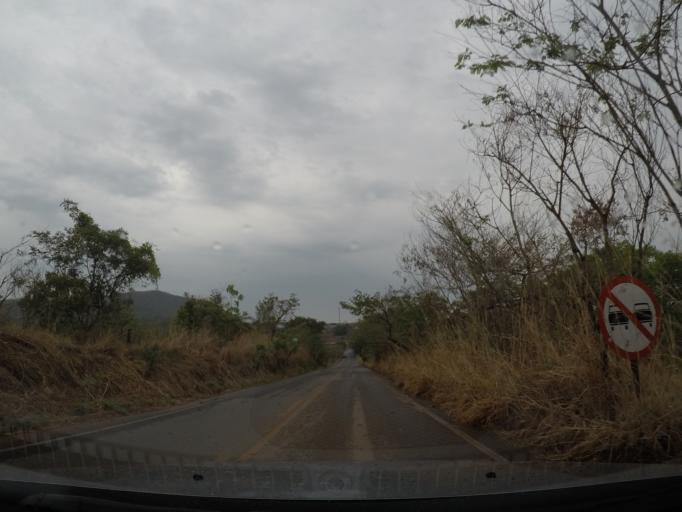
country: BR
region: Goias
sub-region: Pirenopolis
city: Pirenopolis
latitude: -15.8524
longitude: -48.9360
